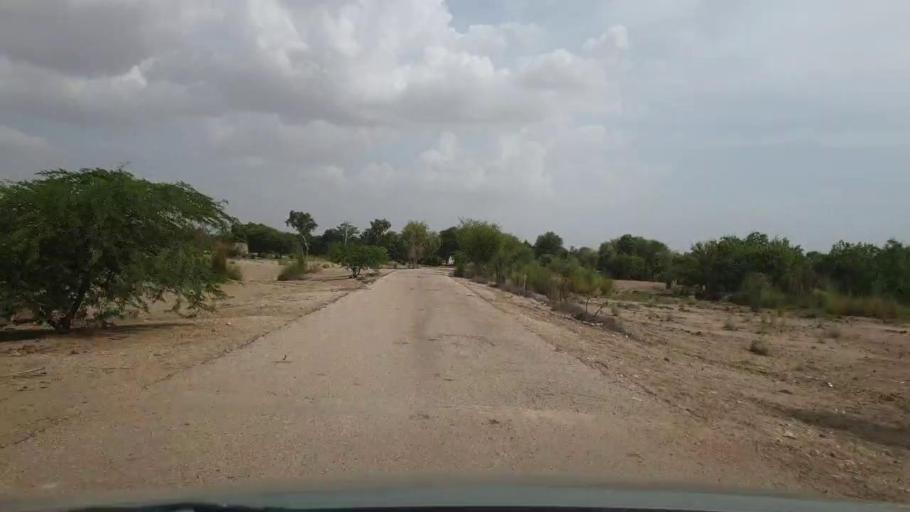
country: PK
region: Sindh
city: Bozdar
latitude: 27.0851
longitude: 69.0138
